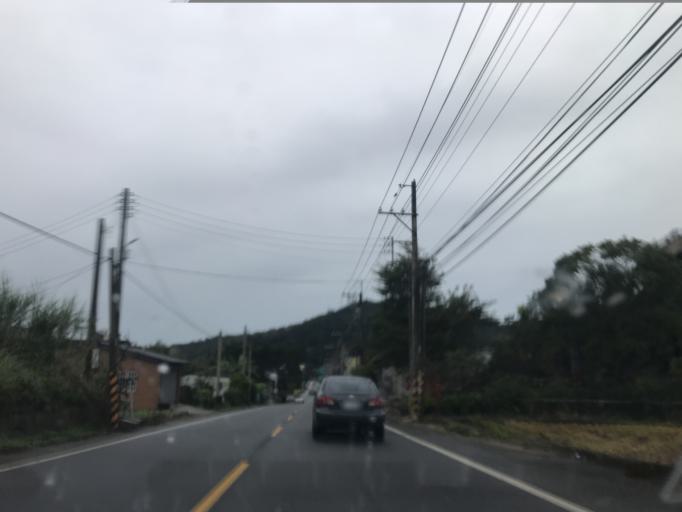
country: TW
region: Taiwan
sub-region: Hsinchu
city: Zhubei
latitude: 24.8391
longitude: 121.1047
